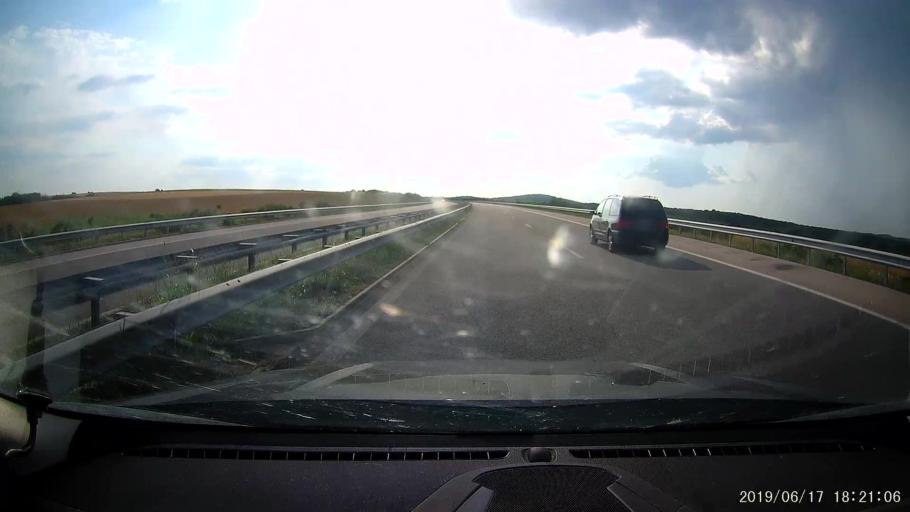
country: BG
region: Khaskovo
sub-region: Obshtina Simeonovgrad
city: Simeonovgrad
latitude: 41.9667
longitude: 25.7935
